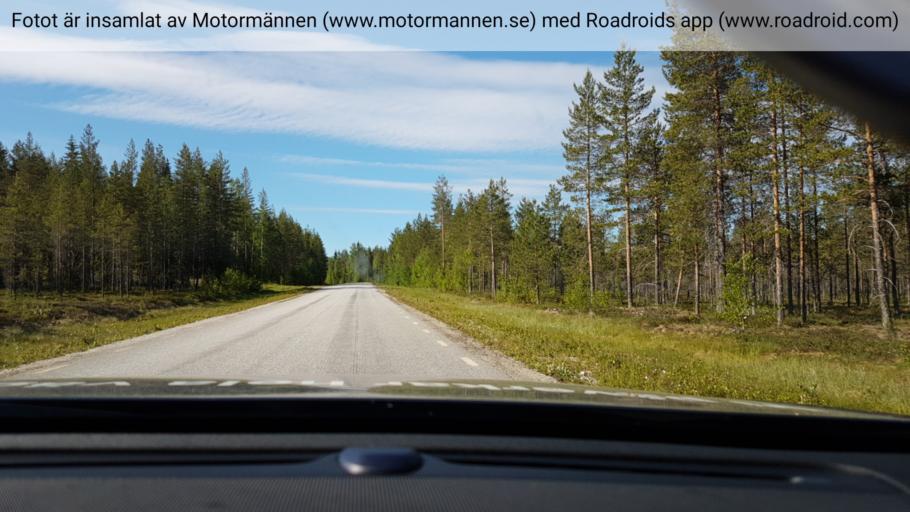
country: SE
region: Vaesterbotten
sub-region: Bjurholms Kommun
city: Bjurholm
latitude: 64.0665
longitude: 19.3375
